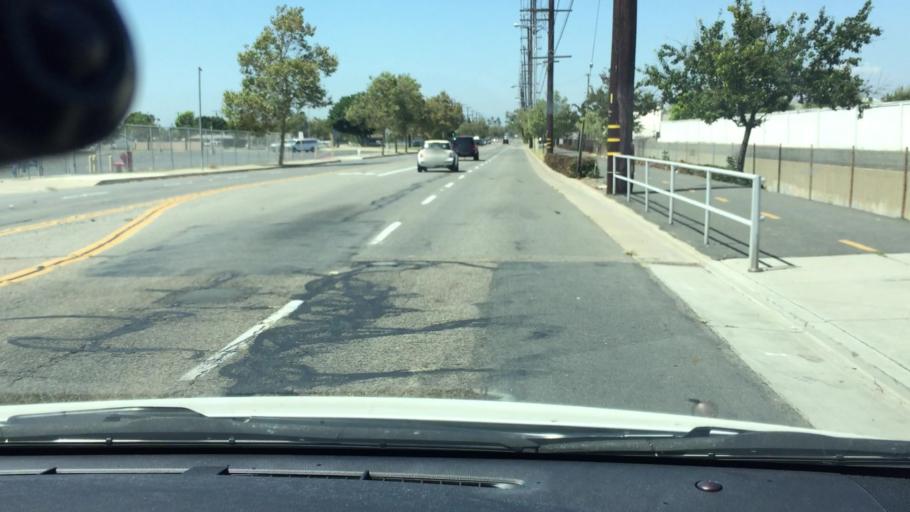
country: US
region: California
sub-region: Orange County
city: Santa Ana
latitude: 33.7076
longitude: -117.8768
